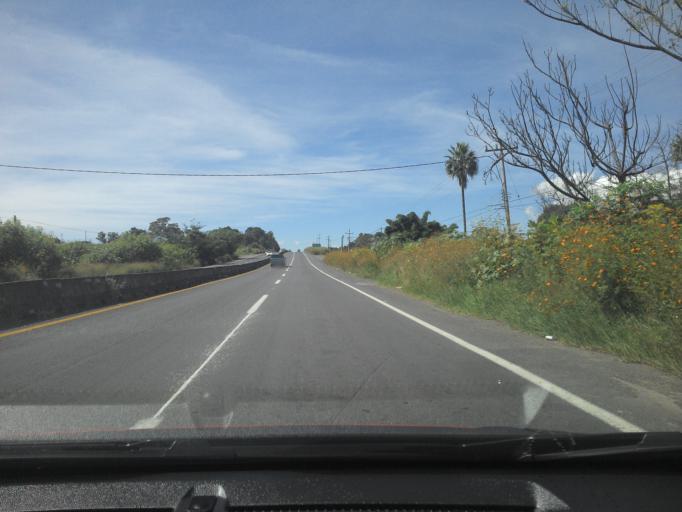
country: MX
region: Jalisco
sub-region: Tala
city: Los Ruisenores
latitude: 20.7178
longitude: -103.6364
